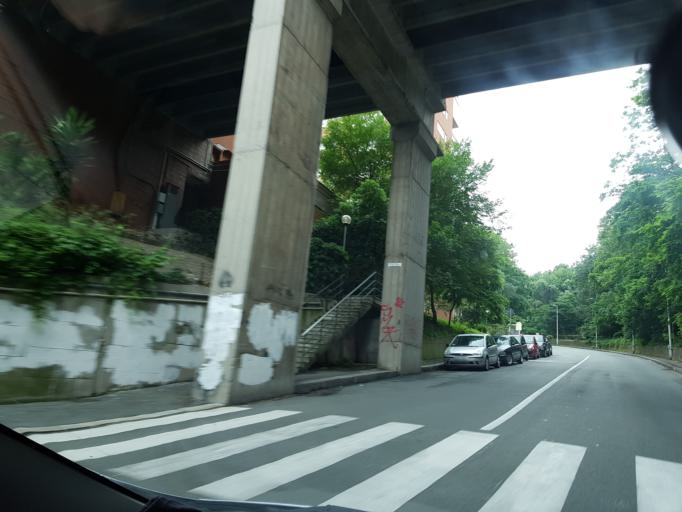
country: IT
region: Liguria
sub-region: Provincia di Genova
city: Genoa
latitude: 44.4246
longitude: 8.9087
